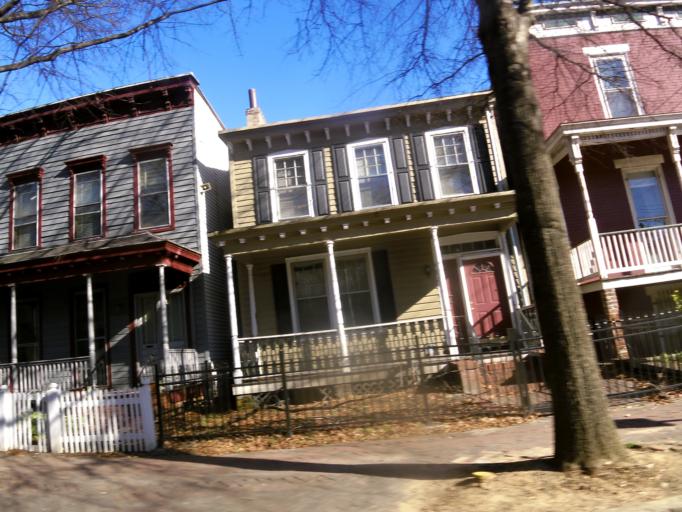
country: US
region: Virginia
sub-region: City of Richmond
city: Richmond
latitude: 37.5488
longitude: -77.4448
